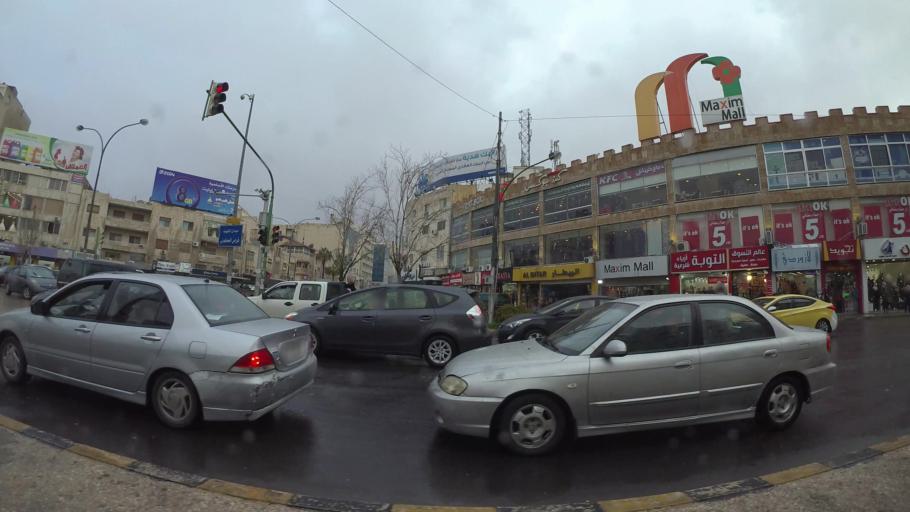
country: JO
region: Amman
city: Amman
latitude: 31.9676
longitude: 35.9180
